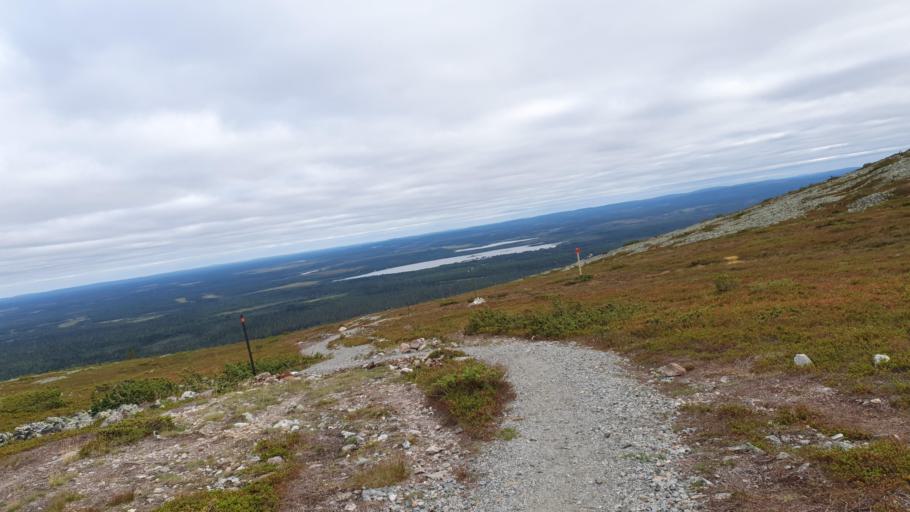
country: FI
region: Lapland
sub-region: Tunturi-Lappi
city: Kolari
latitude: 67.5669
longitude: 24.2479
